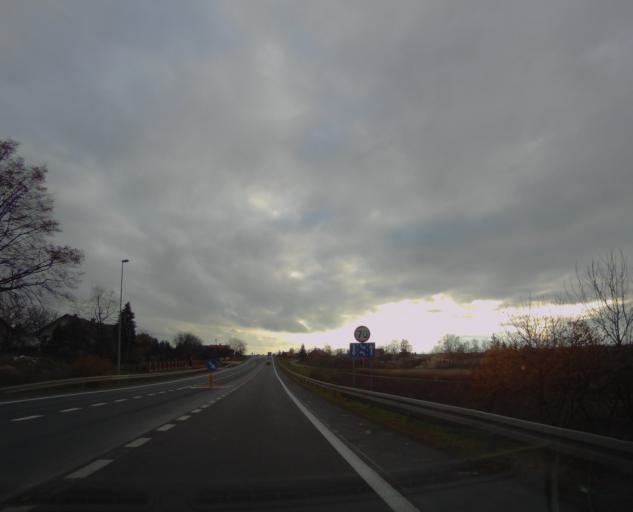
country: PL
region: Subcarpathian Voivodeship
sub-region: Powiat jaroslawski
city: Radymno
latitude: 49.9267
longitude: 22.8214
